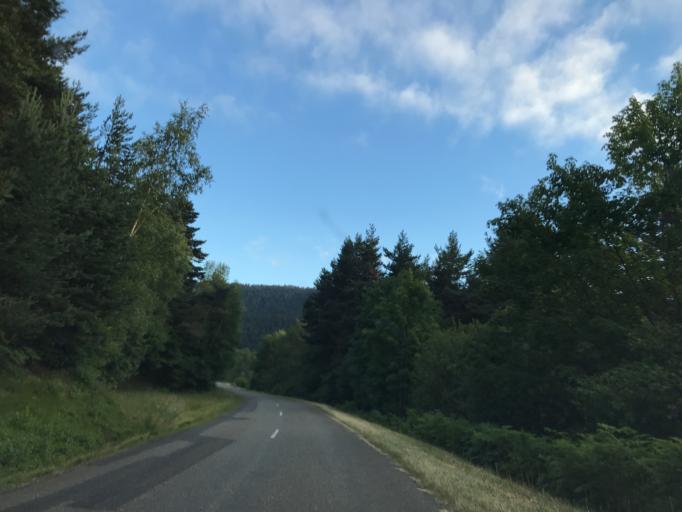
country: FR
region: Rhone-Alpes
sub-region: Departement de la Loire
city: Noiretable
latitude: 45.7597
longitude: 3.8284
